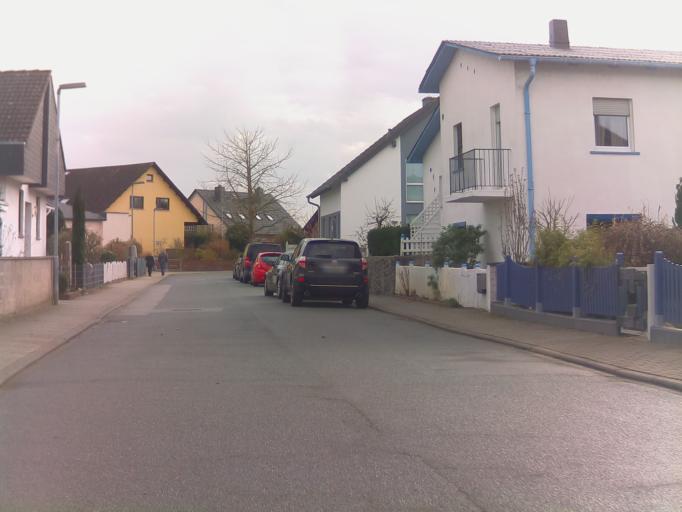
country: DE
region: Hesse
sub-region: Regierungsbezirk Darmstadt
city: Alsbach-Hahnlein
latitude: 49.7358
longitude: 8.5684
